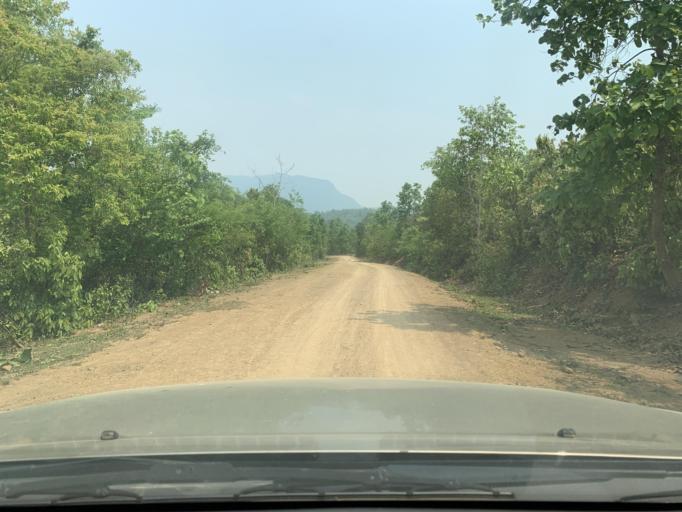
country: LA
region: Louangphabang
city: Louangphabang
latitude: 19.9382
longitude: 102.1324
